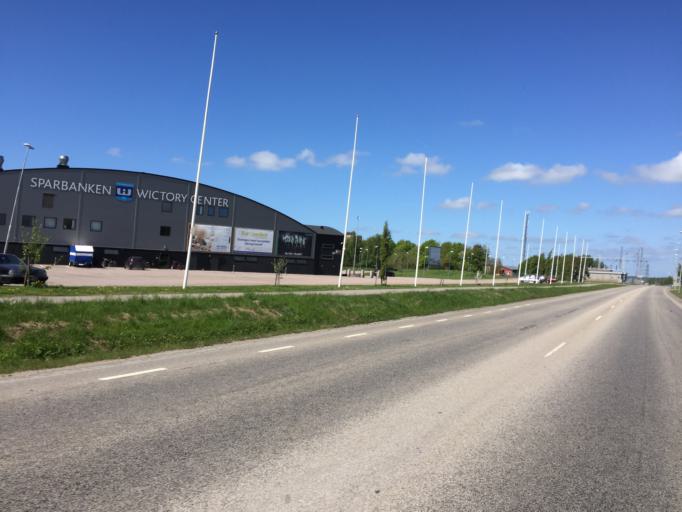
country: SE
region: Halland
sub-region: Varbergs Kommun
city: Varberg
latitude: 57.1164
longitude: 12.2903
